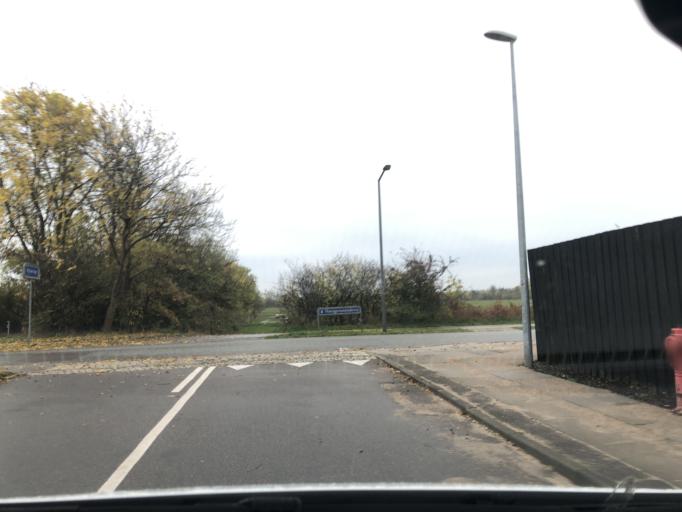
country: DK
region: Capital Region
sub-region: Tarnby Kommune
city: Tarnby
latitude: 55.5926
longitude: 12.5909
